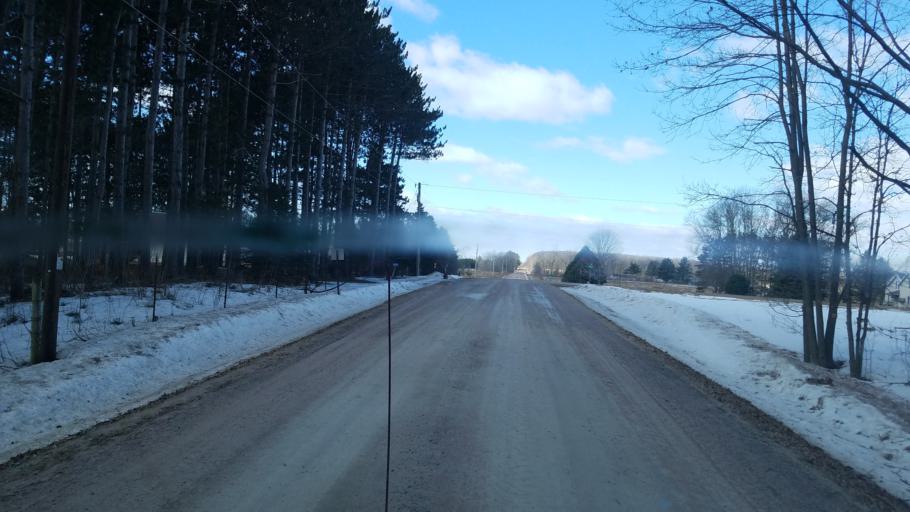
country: US
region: Wisconsin
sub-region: Clark County
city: Loyal
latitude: 44.6256
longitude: -90.4161
